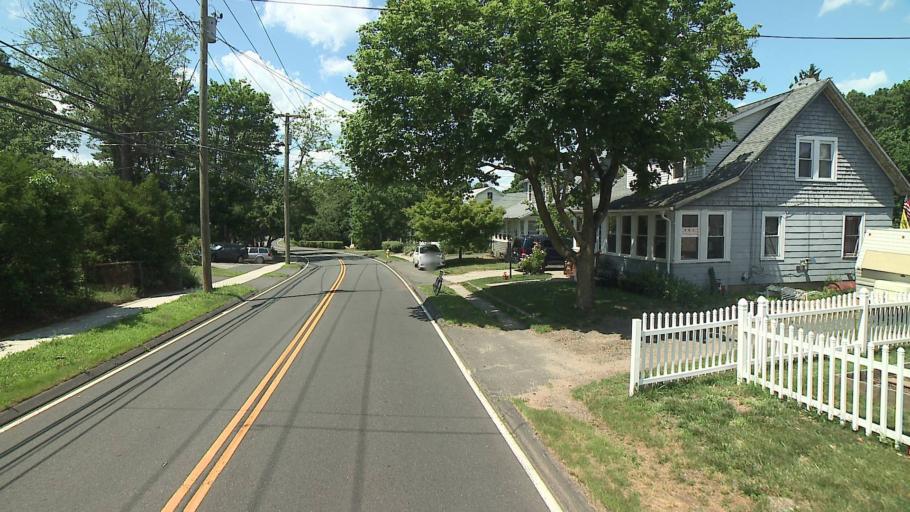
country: US
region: Connecticut
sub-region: New Haven County
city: City of Milford (balance)
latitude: 41.2149
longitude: -73.0625
